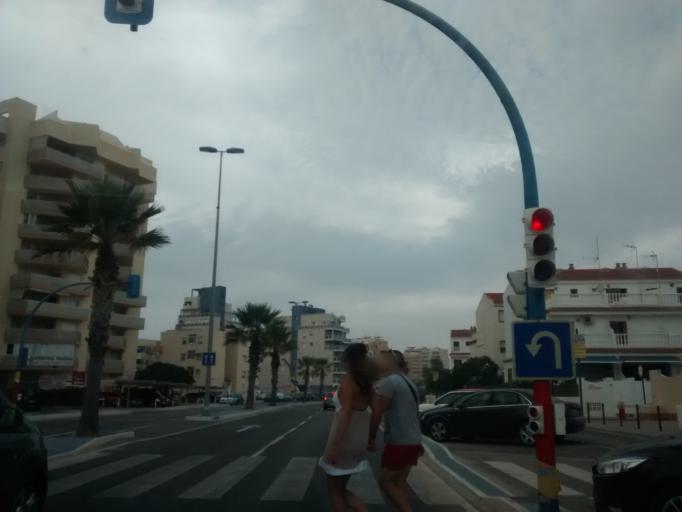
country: ES
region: Murcia
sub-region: Murcia
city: La Manga del Mar Menor
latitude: 37.7066
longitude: -0.7424
